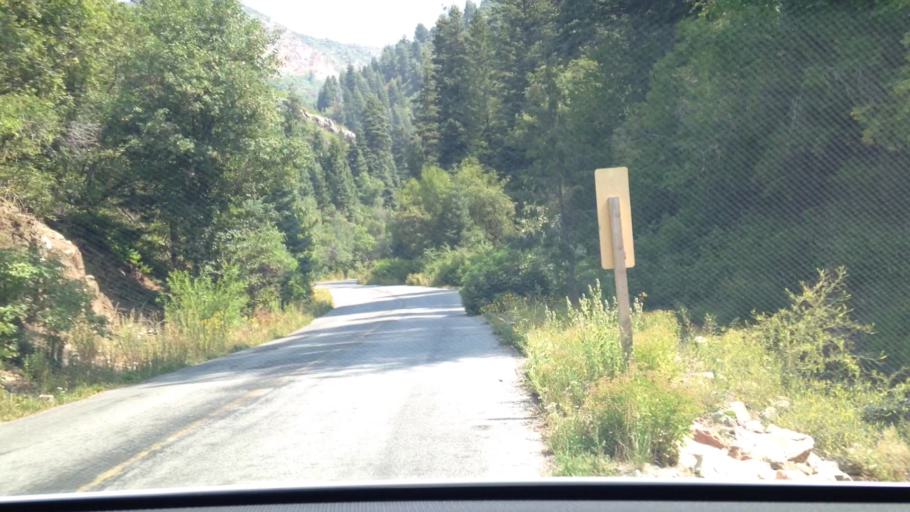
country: US
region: Utah
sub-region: Summit County
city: Summit Park
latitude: 40.7049
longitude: -111.6937
